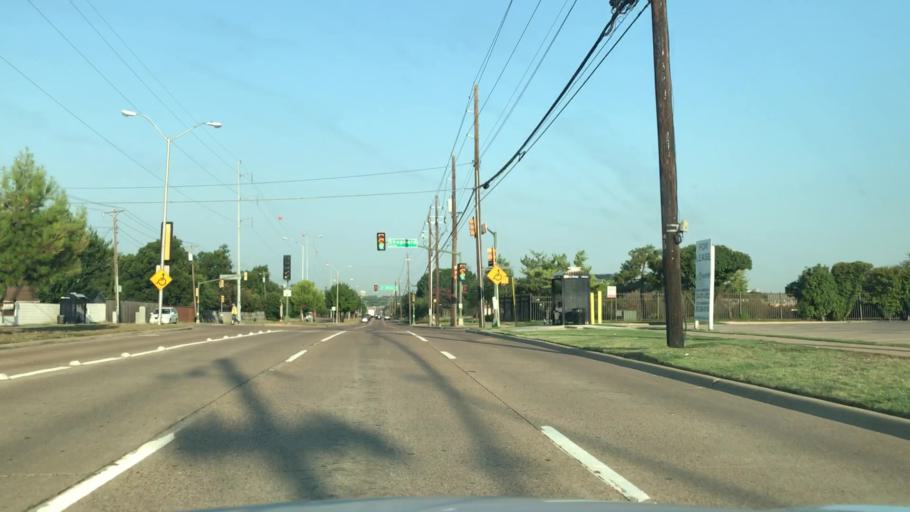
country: US
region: Texas
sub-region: Dallas County
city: Richardson
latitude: 32.9092
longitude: -96.7497
